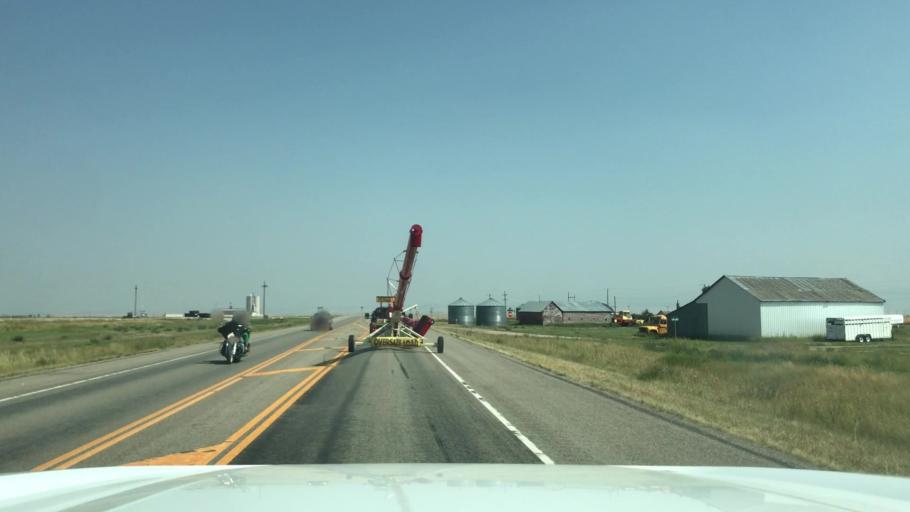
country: US
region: Montana
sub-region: Judith Basin County
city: Stanford
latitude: 47.0539
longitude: -109.9083
